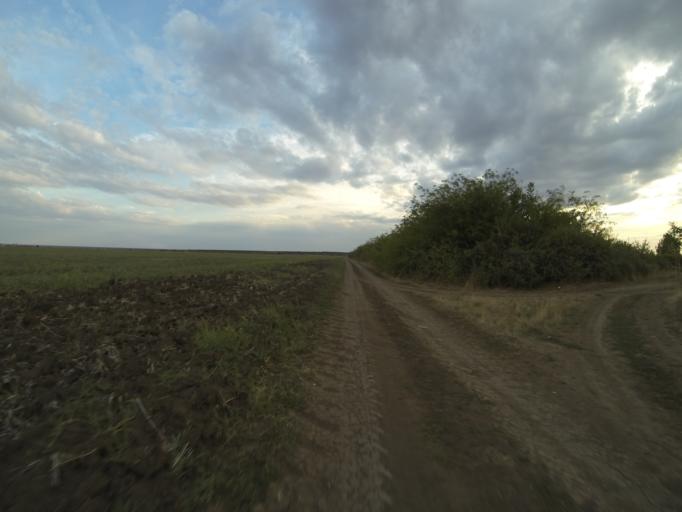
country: RO
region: Dolj
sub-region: Comuna Ceratu
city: Ceratu
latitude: 44.1023
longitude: 23.6921
